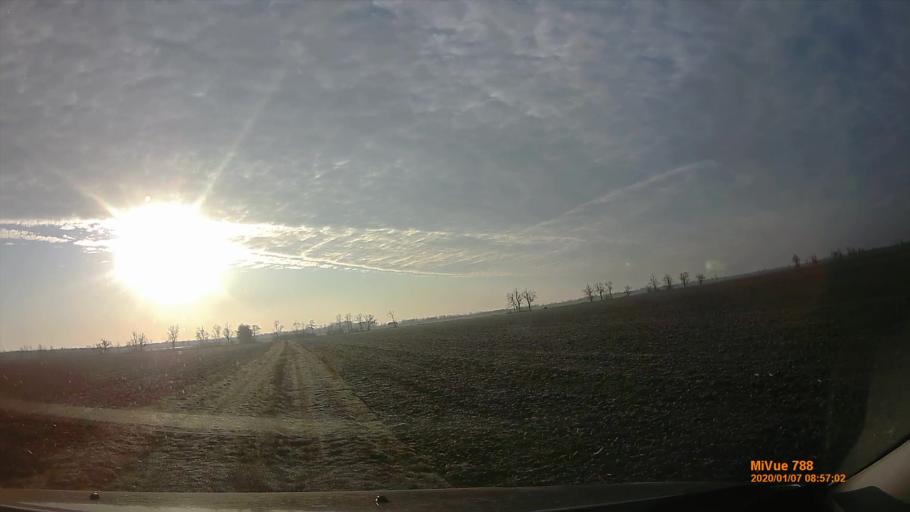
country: HU
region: Gyor-Moson-Sopron
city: Rajka
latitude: 47.9881
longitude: 17.1793
